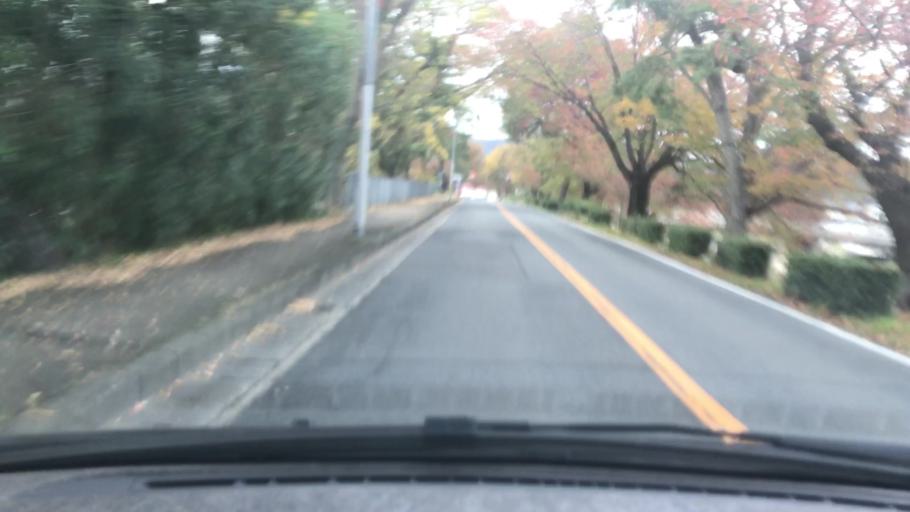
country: JP
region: Kyoto
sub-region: Kyoto-shi
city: Kamigyo-ku
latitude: 35.0486
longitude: 135.7587
